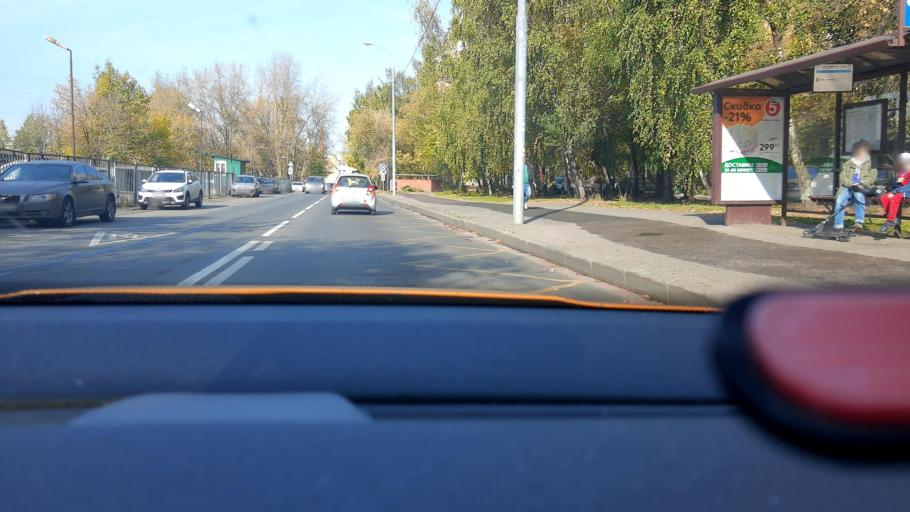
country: RU
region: Moscow
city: Vagonoremont
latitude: 55.8957
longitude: 37.5296
